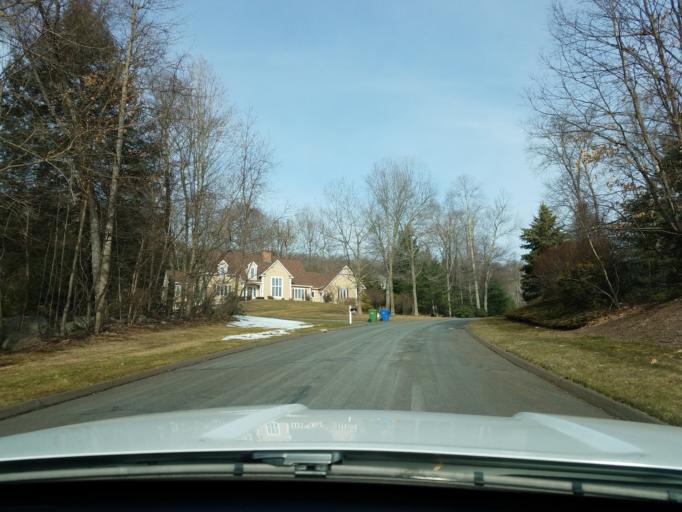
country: US
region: Connecticut
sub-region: Hartford County
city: Collinsville
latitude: 41.7942
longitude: -72.8940
